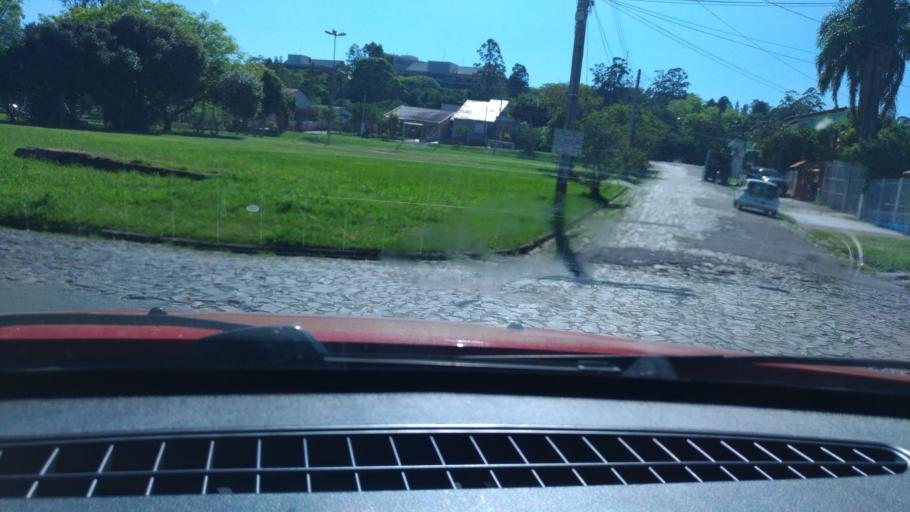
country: BR
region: Rio Grande do Sul
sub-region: Cachoeirinha
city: Cachoeirinha
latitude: -30.0340
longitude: -51.1269
